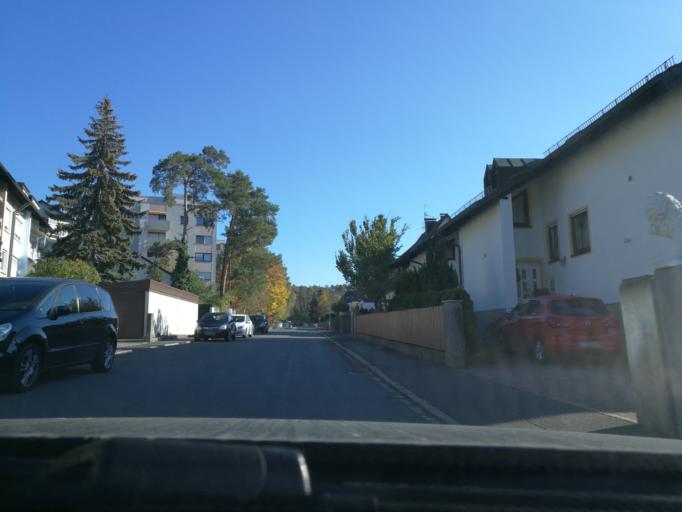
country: DE
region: Bavaria
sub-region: Regierungsbezirk Mittelfranken
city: Zirndorf
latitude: 49.4584
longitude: 10.9305
